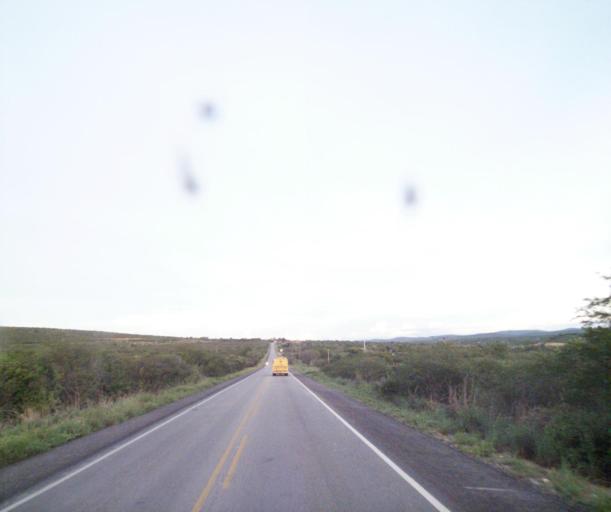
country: BR
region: Bahia
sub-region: Brumado
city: Brumado
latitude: -14.2542
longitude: -41.7511
